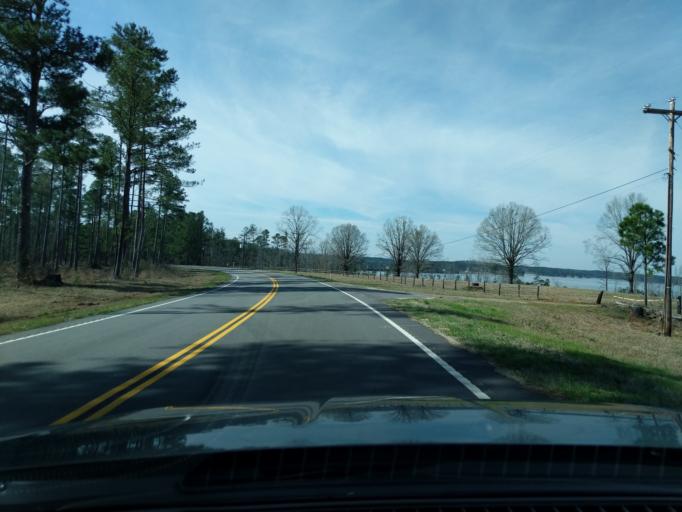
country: US
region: Georgia
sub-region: Columbia County
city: Evans
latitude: 33.6694
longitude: -82.1865
